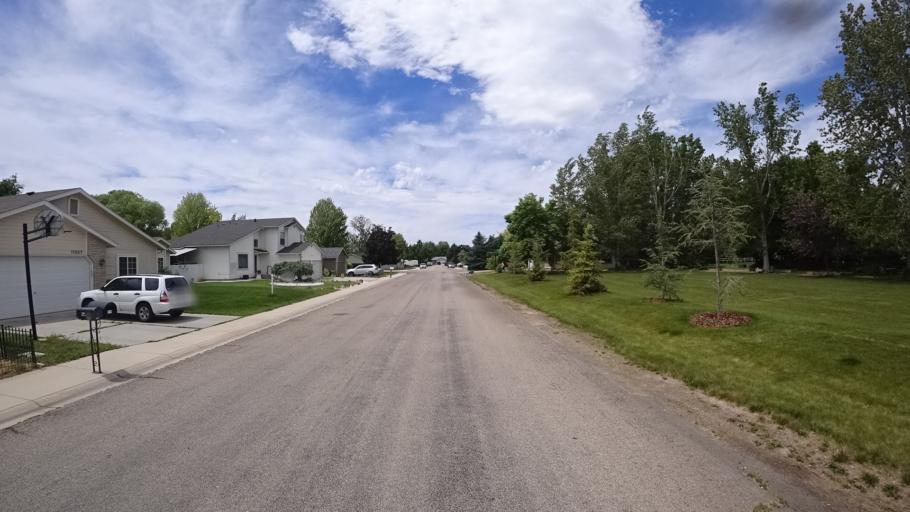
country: US
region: Idaho
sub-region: Ada County
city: Meridian
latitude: 43.6312
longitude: -116.3234
